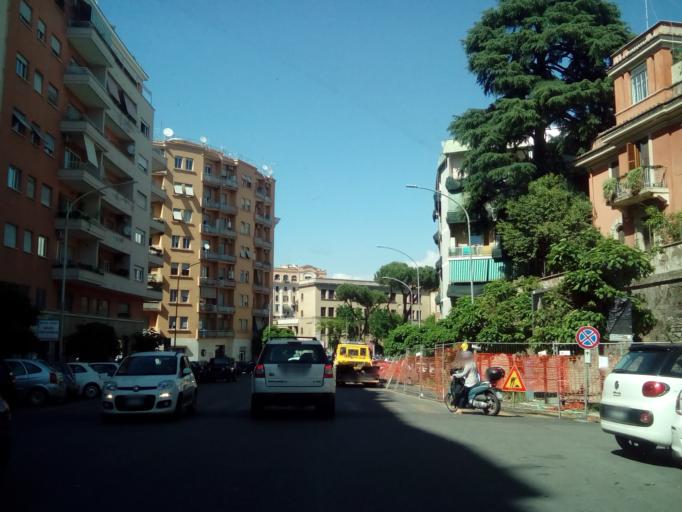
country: IT
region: Latium
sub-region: Citta metropolitana di Roma Capitale
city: Rome
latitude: 41.8828
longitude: 12.5162
